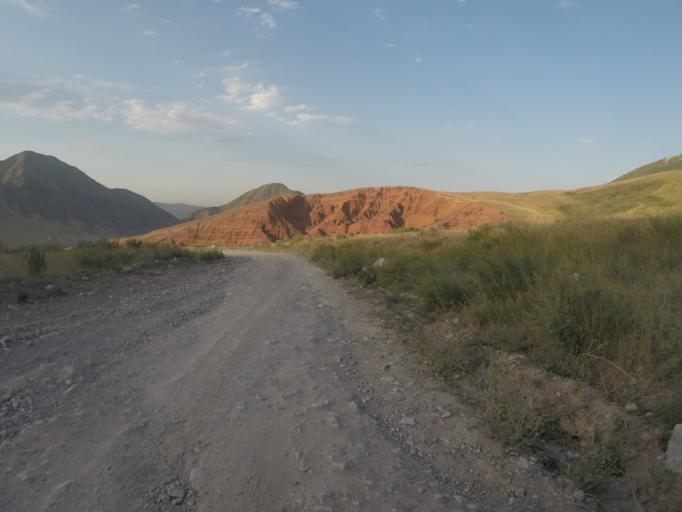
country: KG
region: Chuy
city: Bishkek
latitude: 42.6600
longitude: 74.6517
